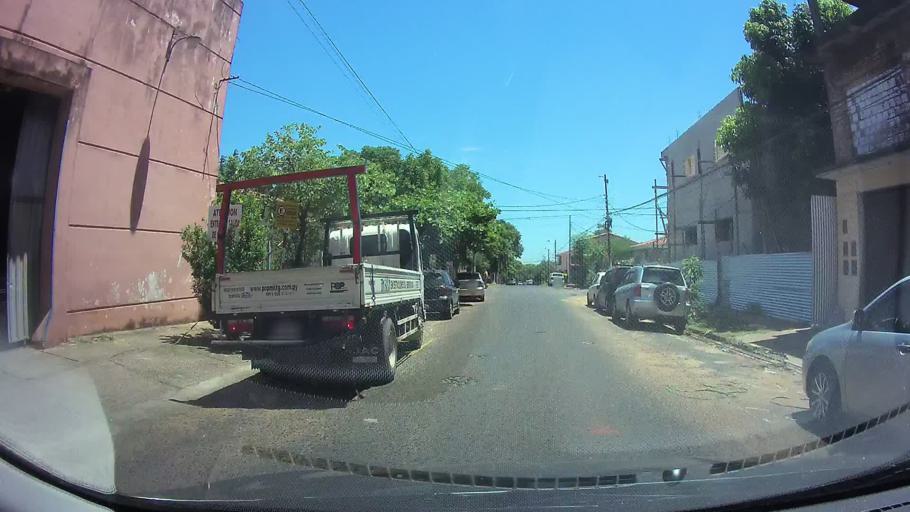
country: PY
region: Central
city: Lambare
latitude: -25.3210
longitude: -57.5916
